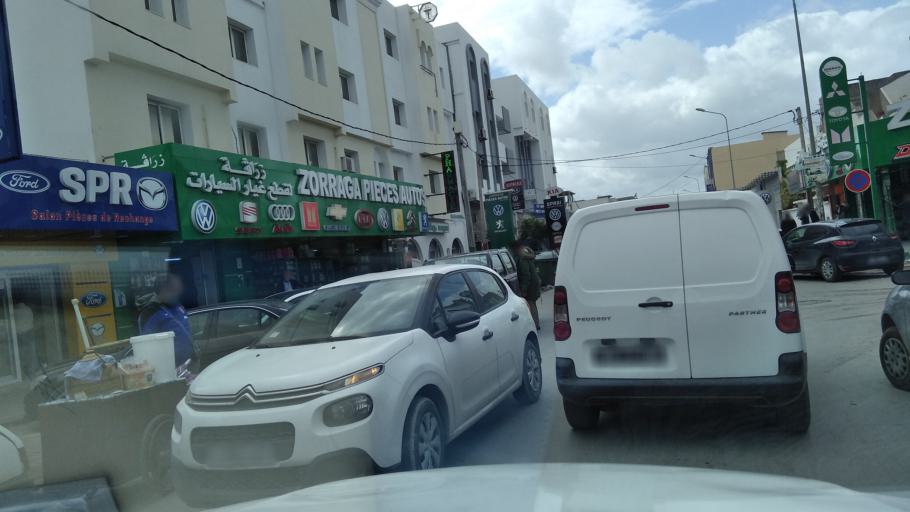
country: TN
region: Bin 'Arus
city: Ben Arous
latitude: 36.7626
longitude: 10.2256
